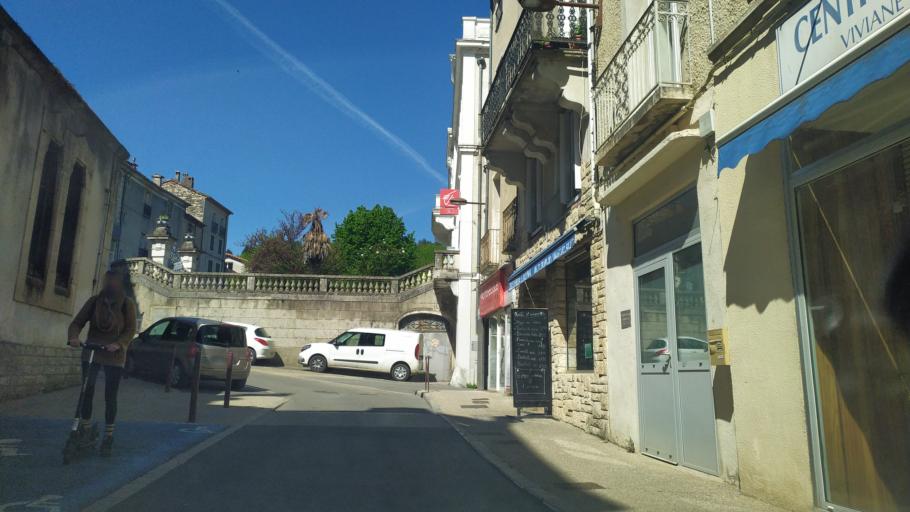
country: FR
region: Languedoc-Roussillon
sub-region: Departement du Gard
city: Le Vigan
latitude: 43.9909
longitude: 3.6053
